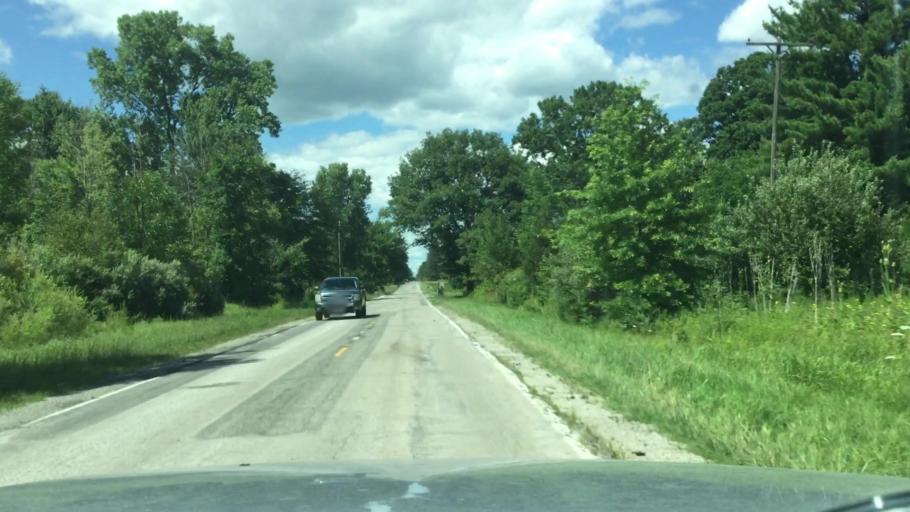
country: US
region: Michigan
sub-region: Saginaw County
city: Hemlock
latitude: 43.3700
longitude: -84.1903
